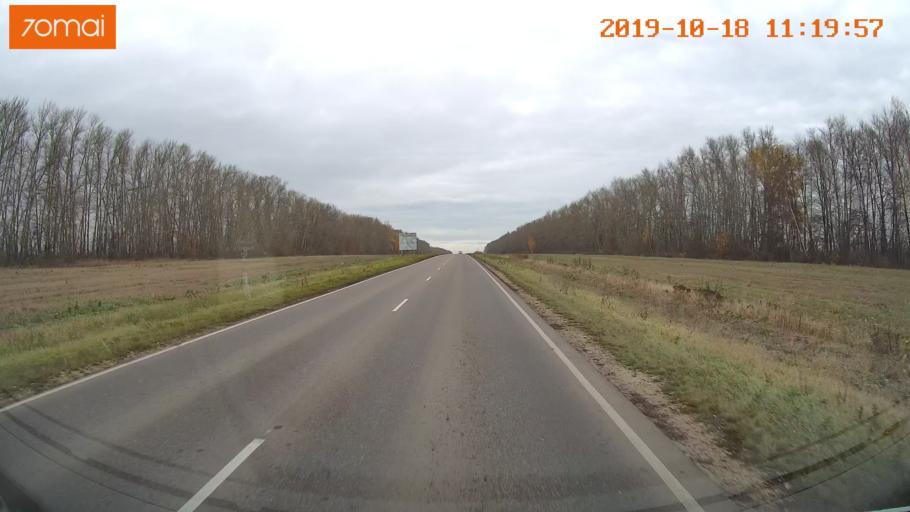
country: RU
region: Tula
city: Kimovsk
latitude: 54.0530
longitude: 38.5563
